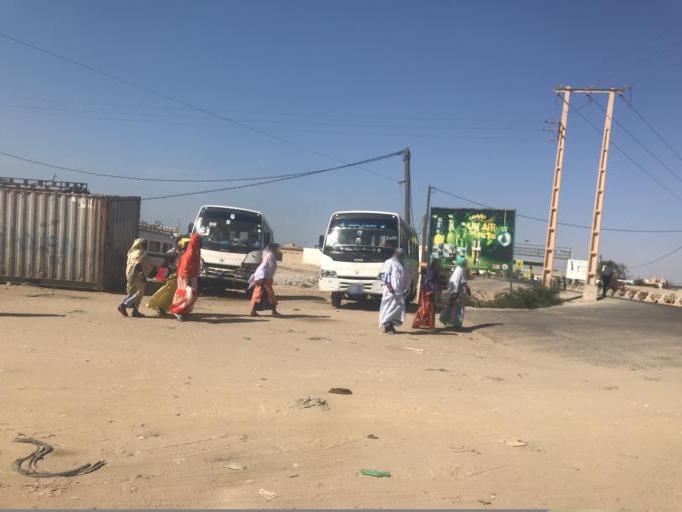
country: SN
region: Saint-Louis
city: Saint-Louis
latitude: 15.9856
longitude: -16.4879
